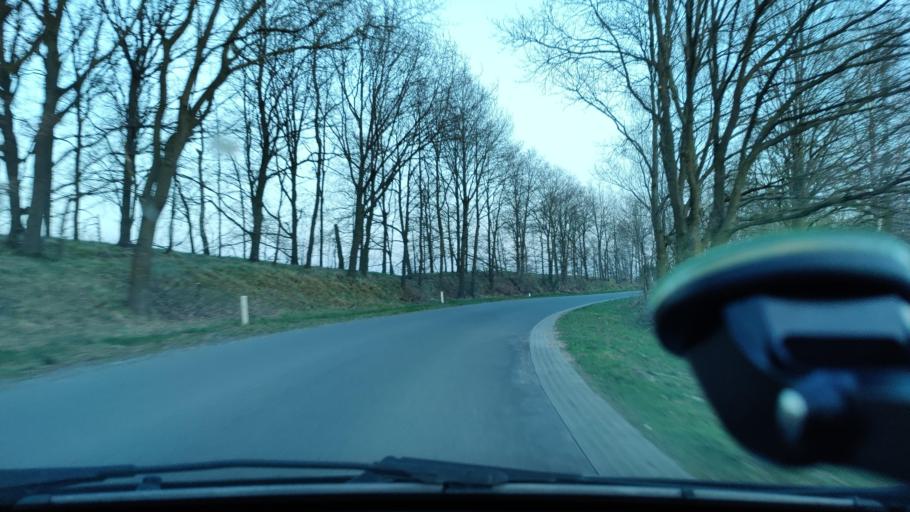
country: NL
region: Limburg
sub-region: Gemeente Bergen
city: Wellerlooi
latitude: 51.5316
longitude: 6.1849
